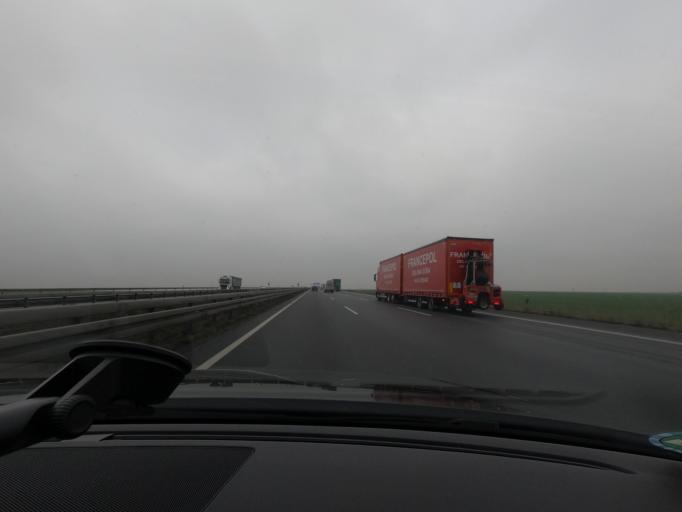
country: DE
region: North Rhine-Westphalia
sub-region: Regierungsbezirk Dusseldorf
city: Juchen
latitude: 51.0690
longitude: 6.4892
